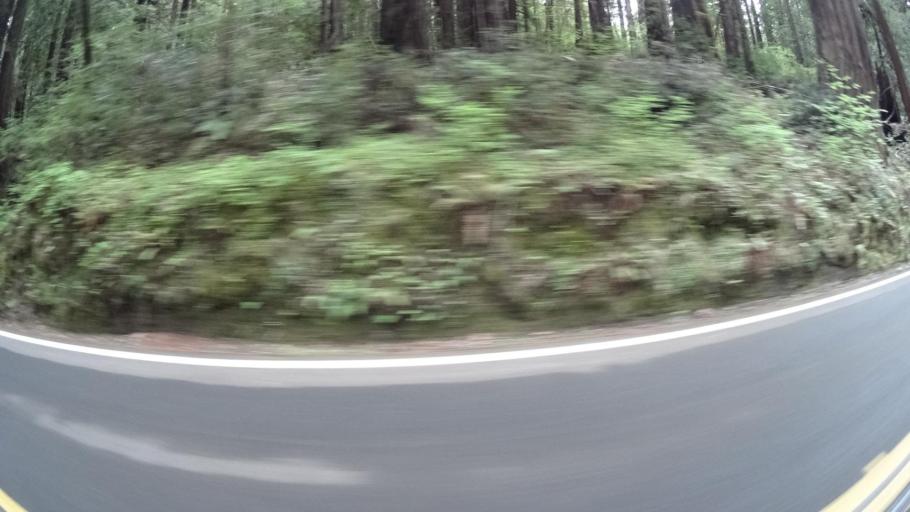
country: US
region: California
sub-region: Humboldt County
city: Redway
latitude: 40.3038
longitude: -123.9022
